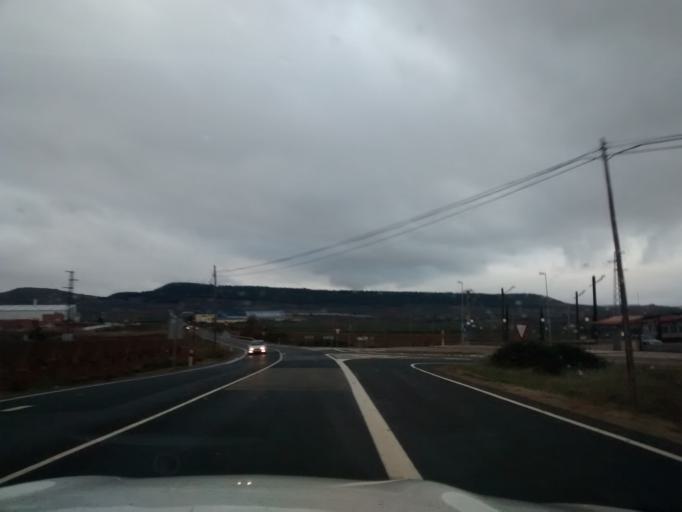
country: ES
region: La Rioja
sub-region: Provincia de La Rioja
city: Fuenmayor
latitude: 42.4612
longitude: -2.5878
